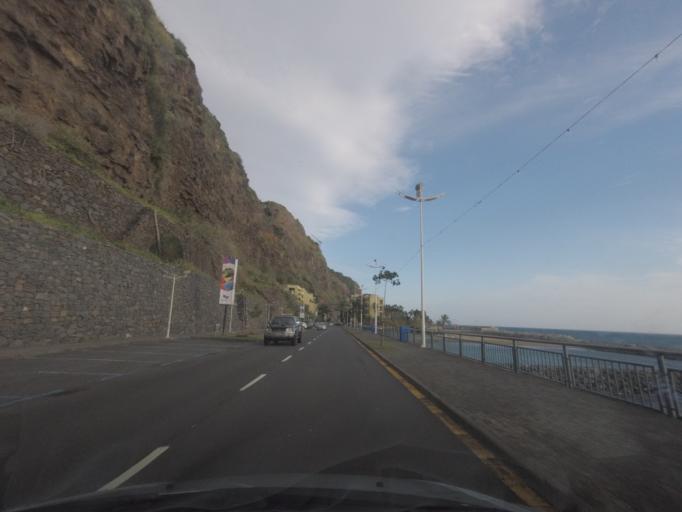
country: PT
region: Madeira
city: Calheta
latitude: 32.7203
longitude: -17.1762
